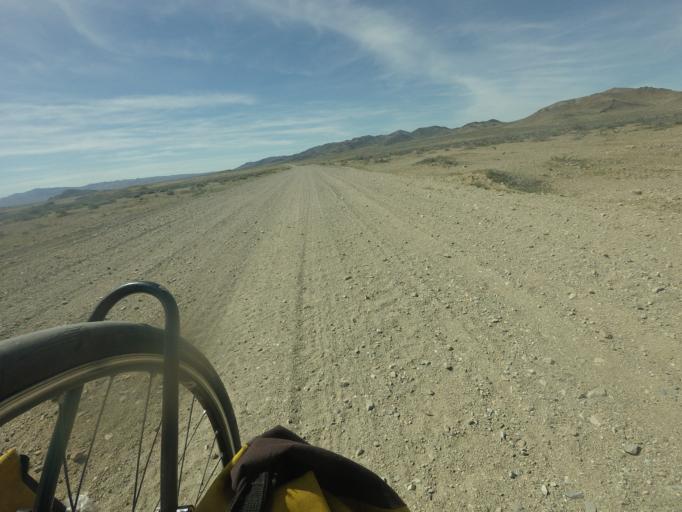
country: US
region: California
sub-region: San Bernardino County
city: Searles Valley
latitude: 35.5959
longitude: -117.4041
